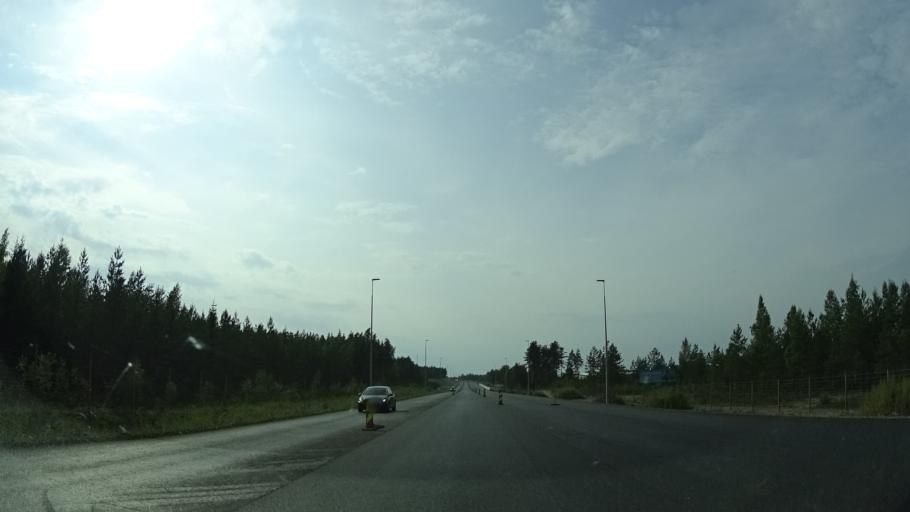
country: FI
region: South Karelia
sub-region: Lappeenranta
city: Luumaeki
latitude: 60.9287
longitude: 27.6062
